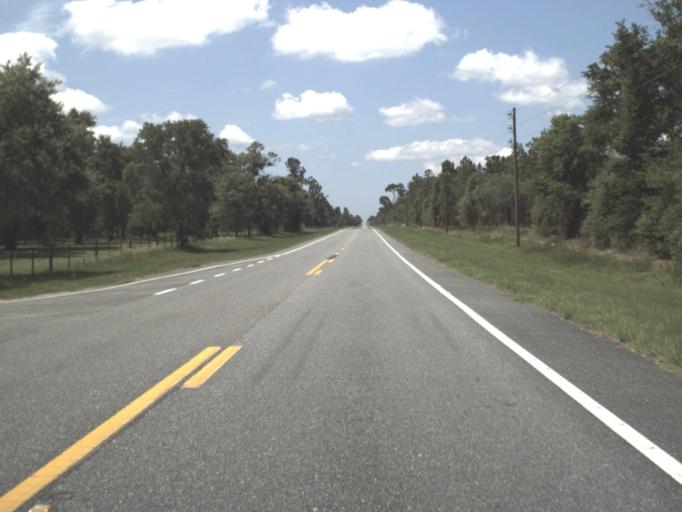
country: US
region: Florida
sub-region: Levy County
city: Williston Highlands
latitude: 29.2735
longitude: -82.5426
